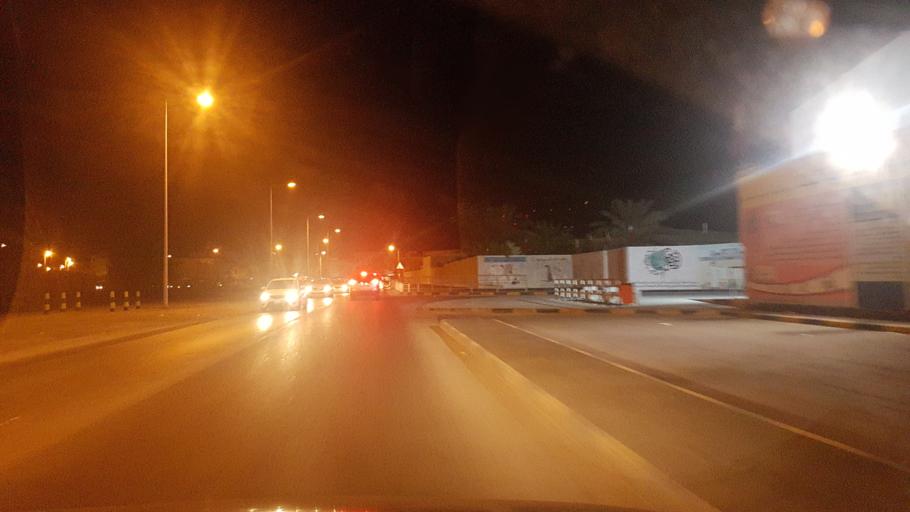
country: BH
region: Muharraq
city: Al Muharraq
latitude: 26.2807
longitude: 50.6284
